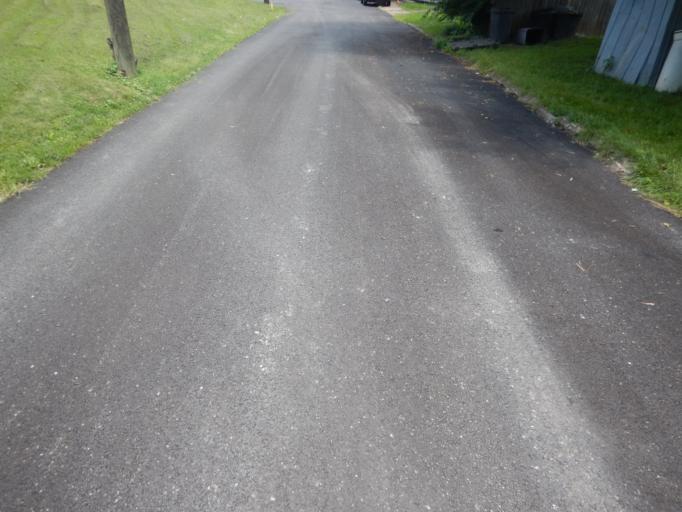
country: US
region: Ohio
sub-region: Muskingum County
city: Zanesville
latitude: 39.9538
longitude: -82.0078
